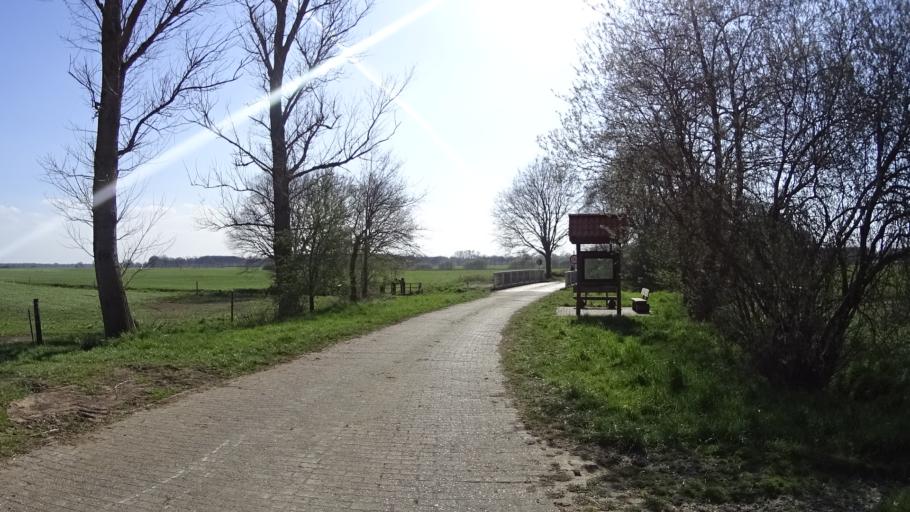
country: DE
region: Lower Saxony
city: Lehe
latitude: 53.0002
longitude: 7.3285
